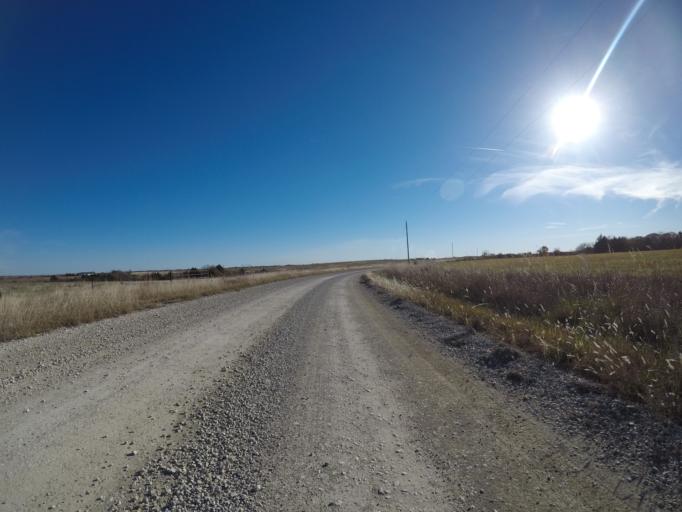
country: US
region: Kansas
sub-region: Riley County
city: Manhattan
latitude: 39.2809
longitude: -96.6786
